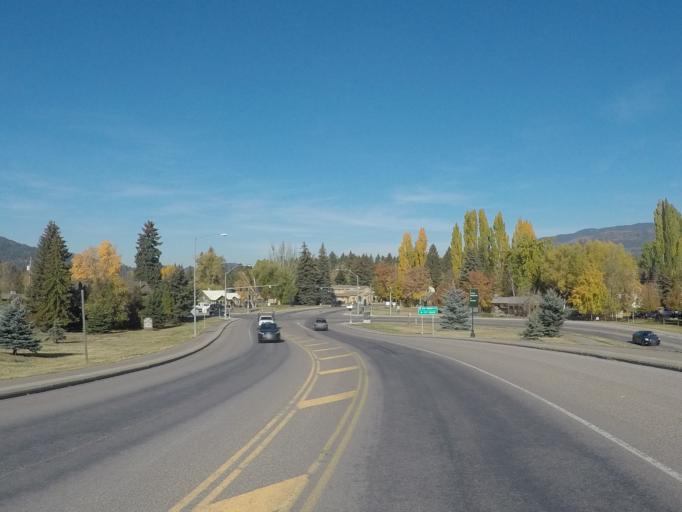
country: US
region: Montana
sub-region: Flathead County
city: Whitefish
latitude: 48.4150
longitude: -114.3393
